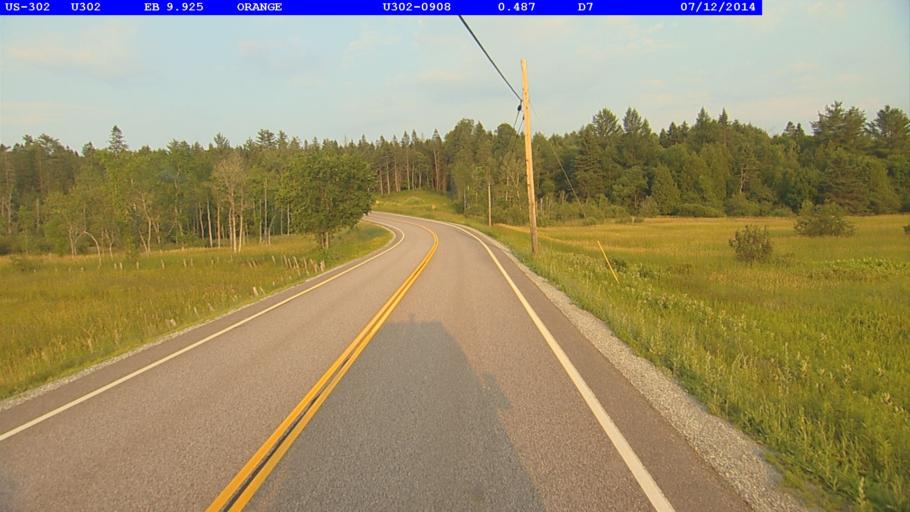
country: US
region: Vermont
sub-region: Washington County
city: South Barre
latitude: 44.1516
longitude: -72.4275
